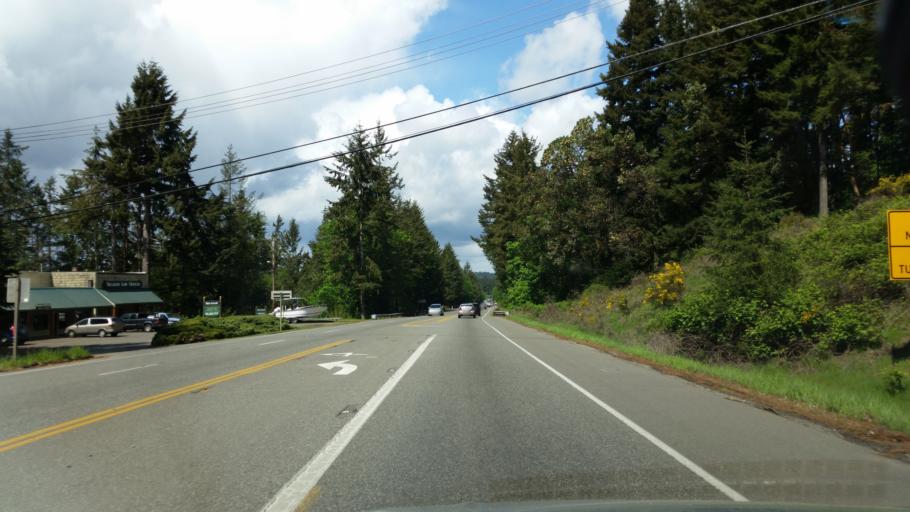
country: US
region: Washington
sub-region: Pierce County
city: Purdy
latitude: 47.3751
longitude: -122.6221
